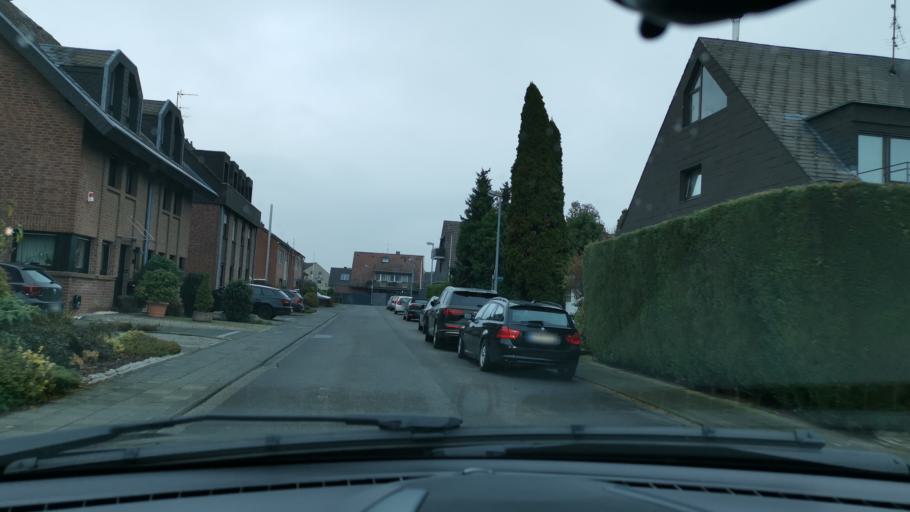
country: DE
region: North Rhine-Westphalia
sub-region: Regierungsbezirk Dusseldorf
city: Neubrueck
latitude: 51.1217
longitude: 6.6768
